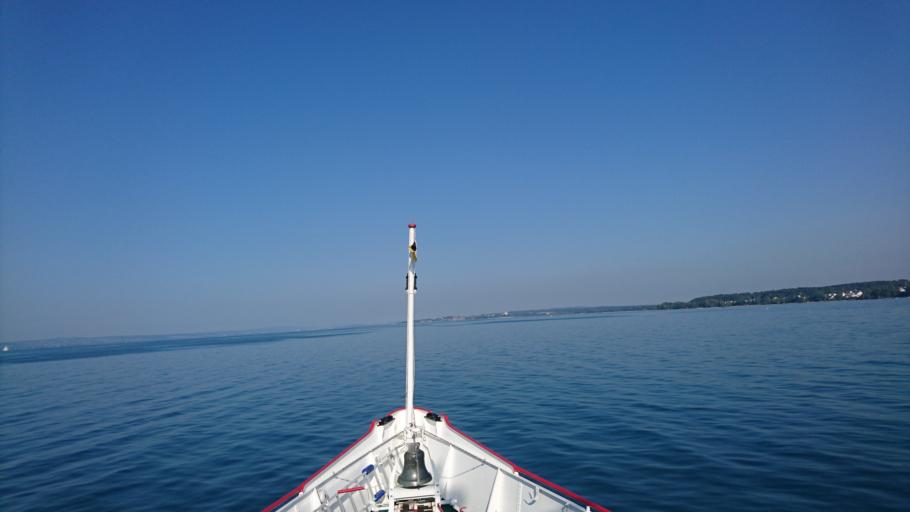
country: DE
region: Baden-Wuerttemberg
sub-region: Tuebingen Region
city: Friedrichshafen
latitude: 47.6447
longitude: 9.4580
